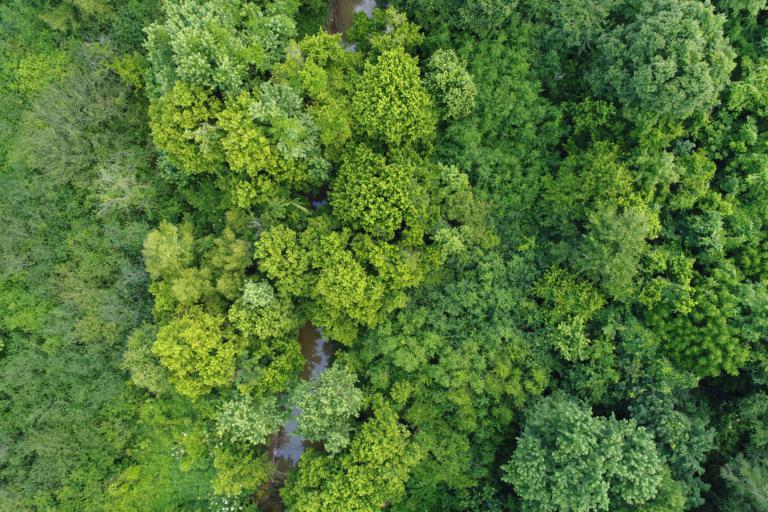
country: US
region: Mississippi
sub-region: De Soto County
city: Walls
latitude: 34.9086
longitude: -90.2066
